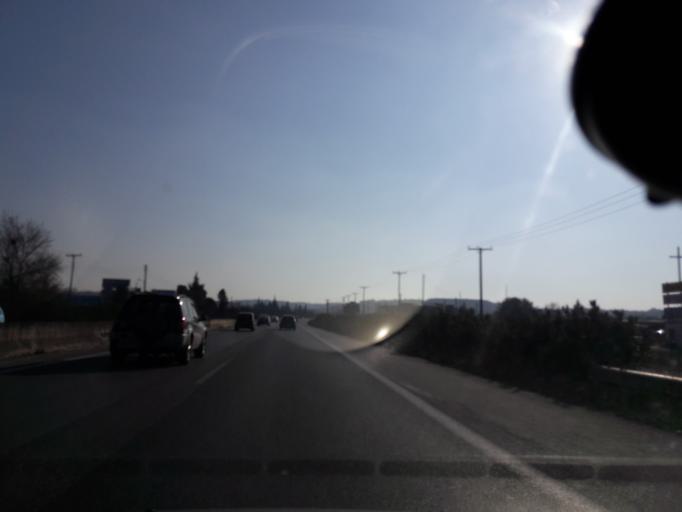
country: GR
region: Central Macedonia
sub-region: Nomos Thessalonikis
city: Neo Rysi
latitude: 40.5037
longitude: 23.0058
